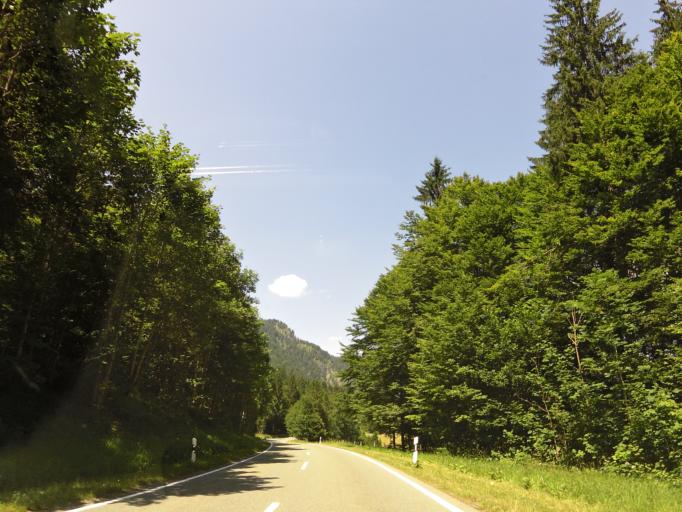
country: DE
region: Bavaria
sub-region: Upper Bavaria
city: Reit im Winkl
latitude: 47.6661
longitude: 12.5441
